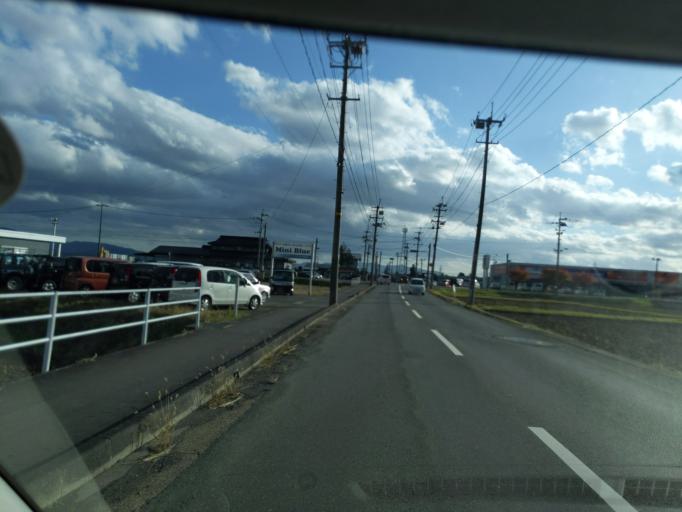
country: JP
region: Iwate
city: Mizusawa
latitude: 39.1541
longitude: 141.1584
